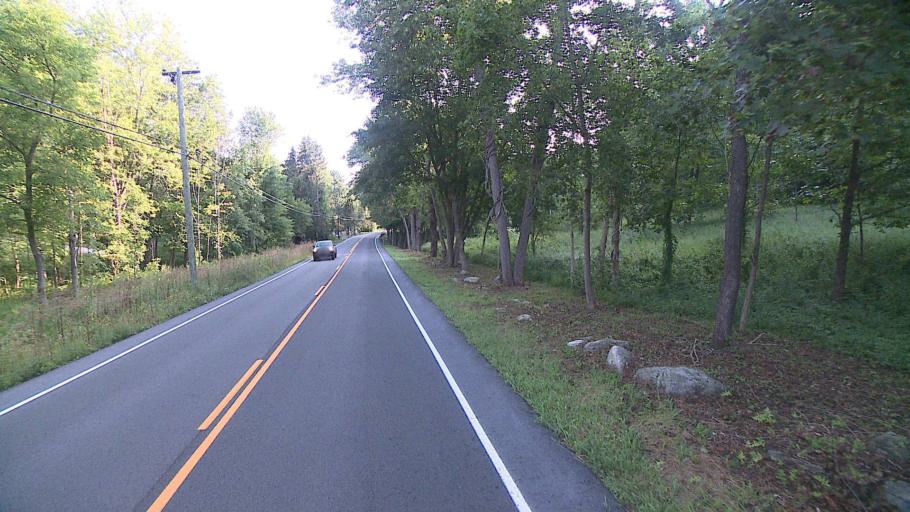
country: US
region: Connecticut
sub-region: Litchfield County
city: Kent
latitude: 41.6982
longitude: -73.4949
